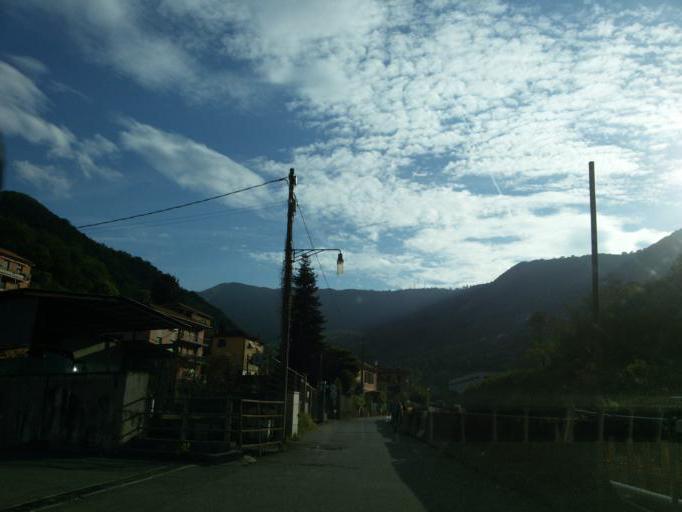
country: IT
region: Liguria
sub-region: Provincia di Genova
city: Piccarello
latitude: 44.4627
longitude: 8.9818
